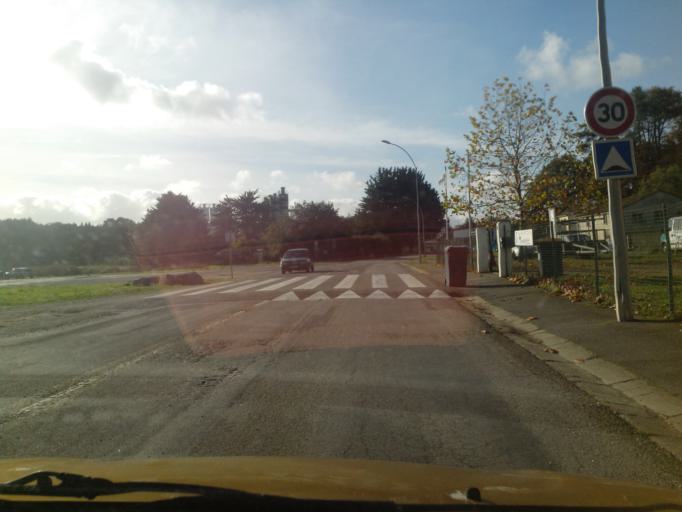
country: FR
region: Brittany
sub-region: Departement du Morbihan
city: Hennebont
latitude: 47.7984
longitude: -3.2777
